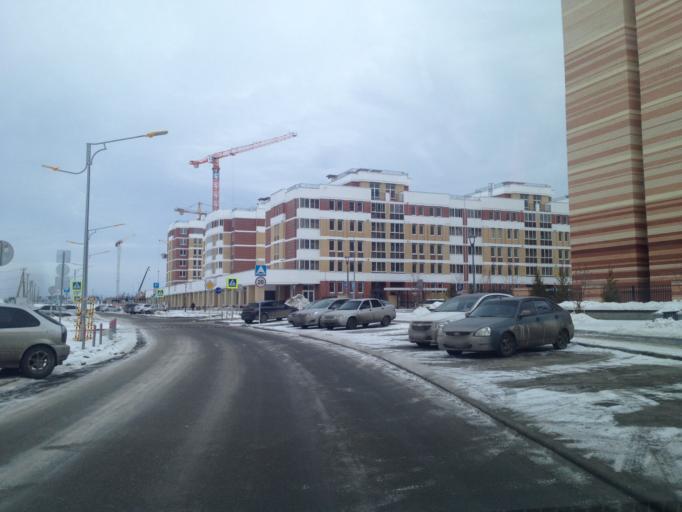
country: RU
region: Sverdlovsk
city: Sovkhoznyy
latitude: 56.7452
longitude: 60.5687
